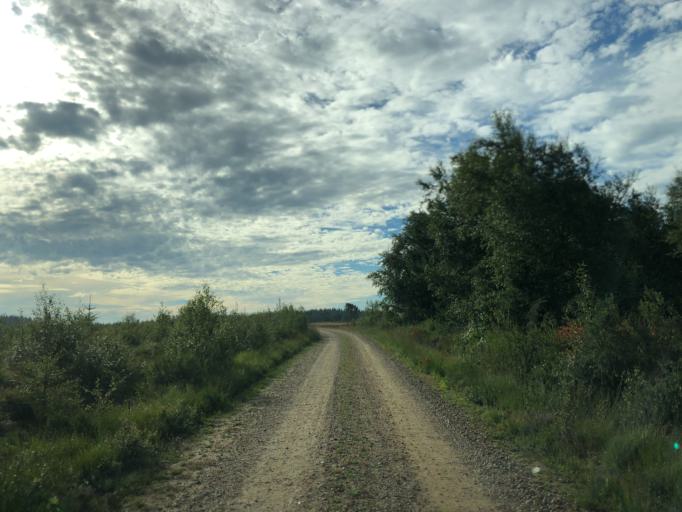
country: DK
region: Central Jutland
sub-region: Holstebro Kommune
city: Ulfborg
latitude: 56.1723
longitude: 8.3760
